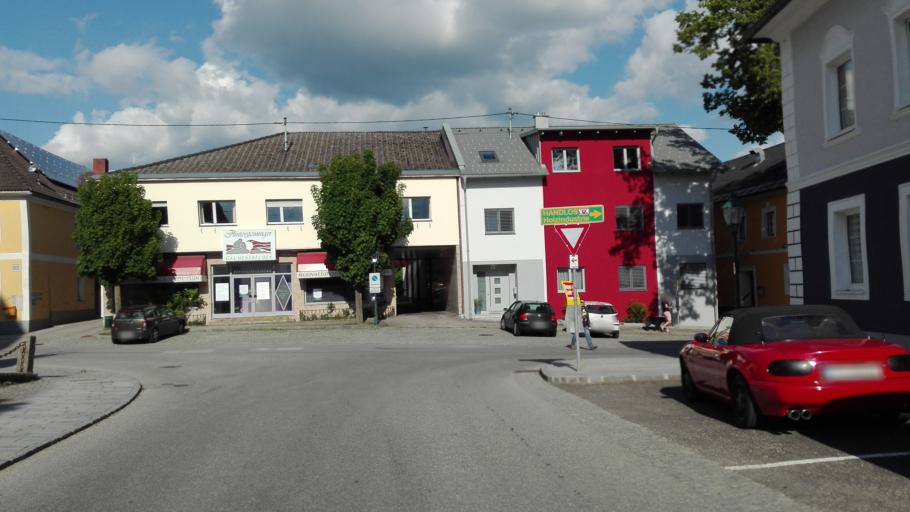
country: AT
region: Upper Austria
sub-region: Politischer Bezirk Perg
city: Perg
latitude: 48.3313
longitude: 14.6217
